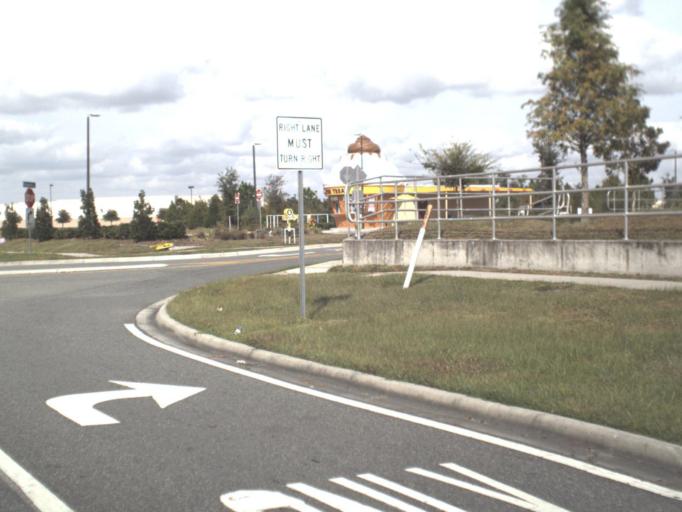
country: US
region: Florida
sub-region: Osceola County
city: Poinciana
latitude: 28.1548
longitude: -81.4413
